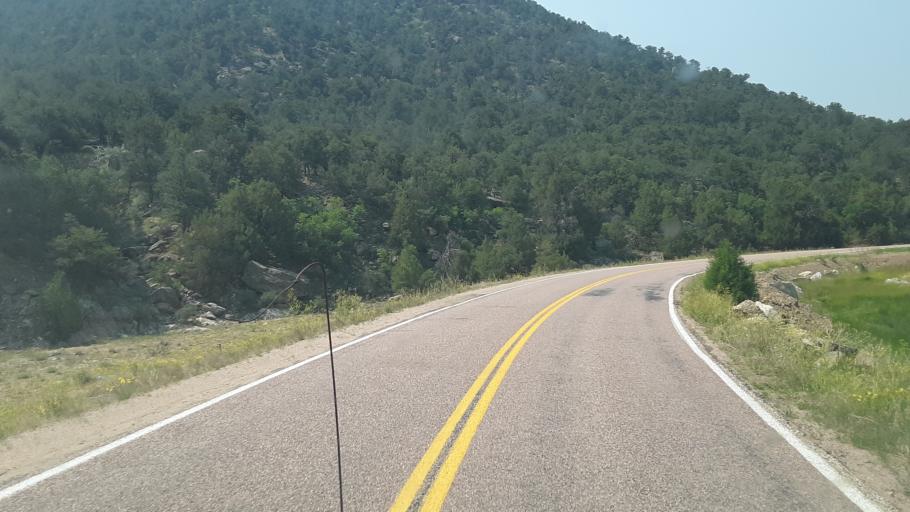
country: US
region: Colorado
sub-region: Fremont County
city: Canon City
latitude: 38.4262
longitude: -105.4025
